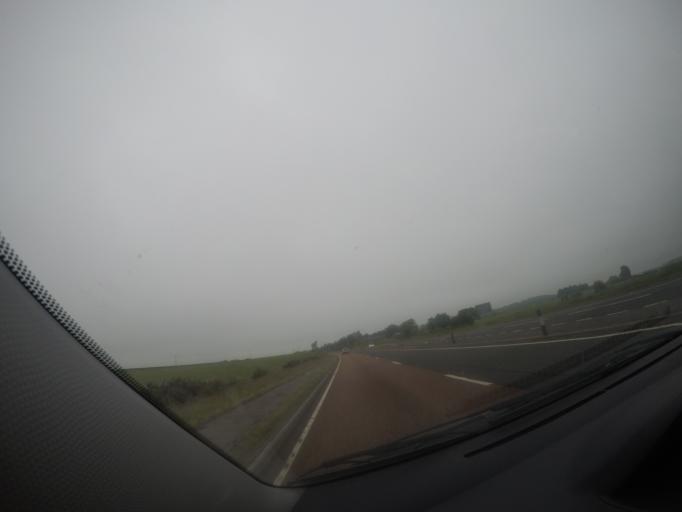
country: GB
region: Scotland
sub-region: Angus
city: Forfar
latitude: 56.6122
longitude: -2.9011
